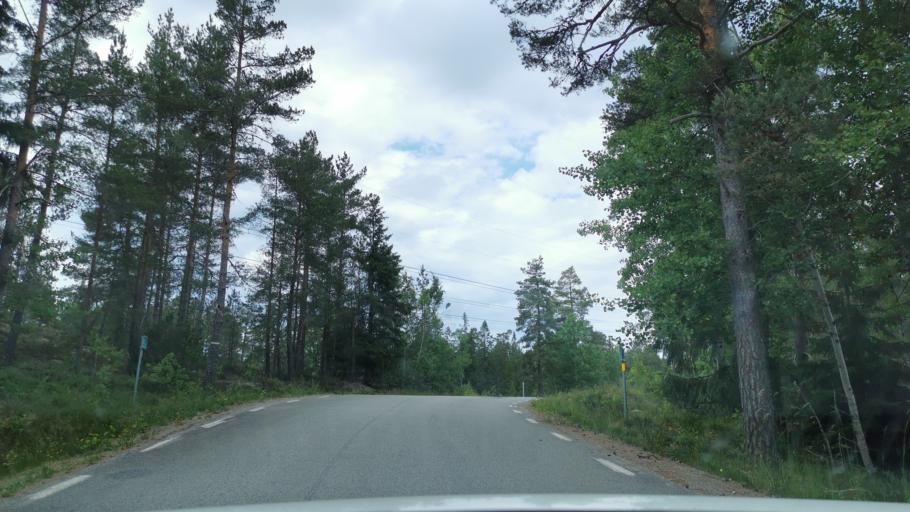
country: SE
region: Vaestra Goetaland
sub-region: Bengtsfors Kommun
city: Dals Langed
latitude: 58.8660
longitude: 12.4029
